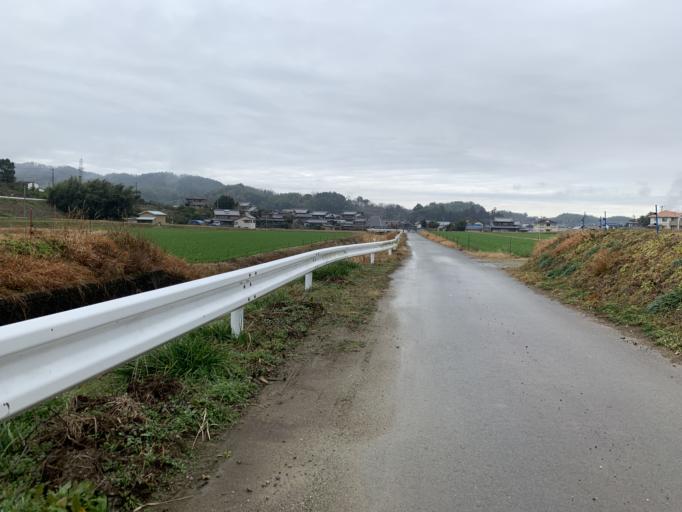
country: JP
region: Mie
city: Ise
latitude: 34.4750
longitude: 136.5466
